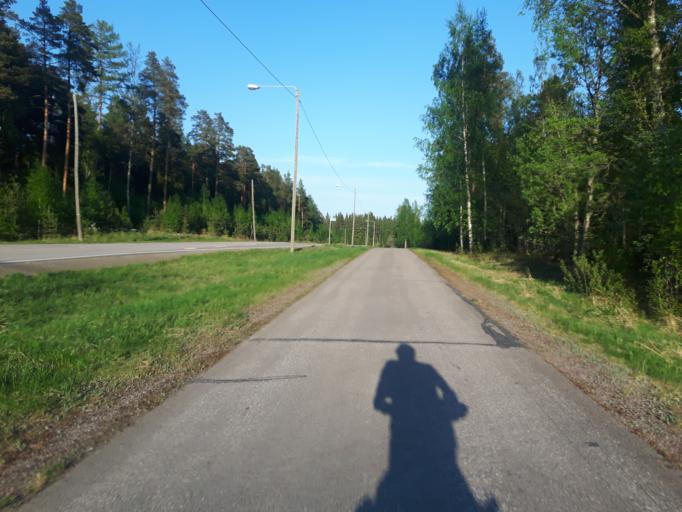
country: FI
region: Uusimaa
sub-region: Loviisa
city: Lovisa
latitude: 60.4562
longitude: 26.1448
